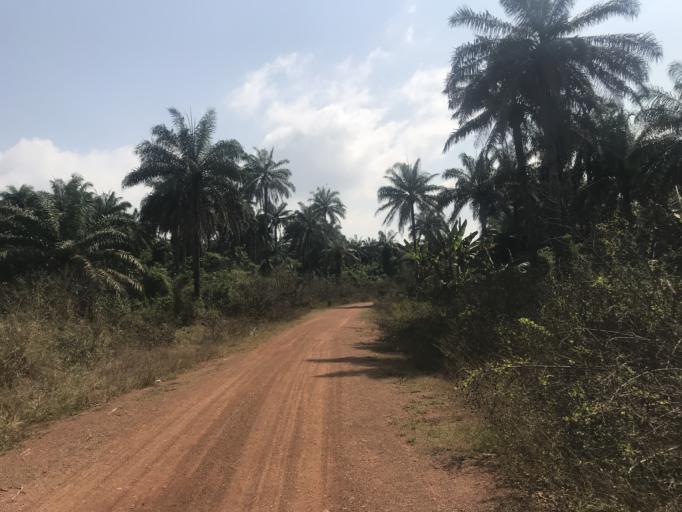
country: NG
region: Osun
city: Ikirun
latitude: 7.8327
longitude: 4.6361
